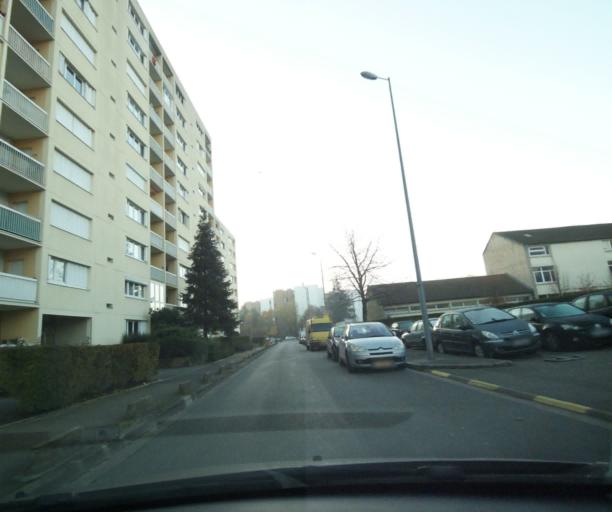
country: FR
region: Ile-de-France
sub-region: Departement de Seine-Saint-Denis
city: Gagny
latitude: 48.8682
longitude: 2.5301
